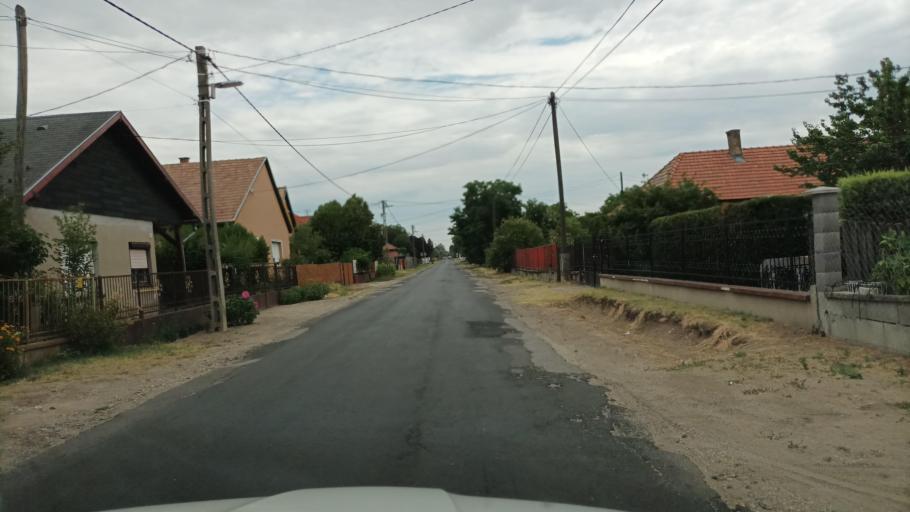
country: HU
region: Pest
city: Taborfalva
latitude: 47.1232
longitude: 19.4844
